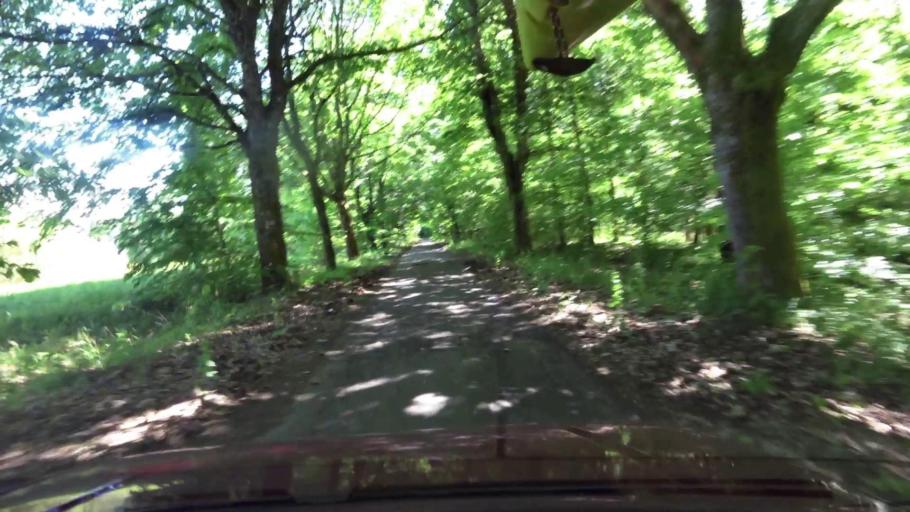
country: PL
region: West Pomeranian Voivodeship
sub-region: Powiat koszalinski
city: Polanow
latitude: 54.0361
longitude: 16.7825
